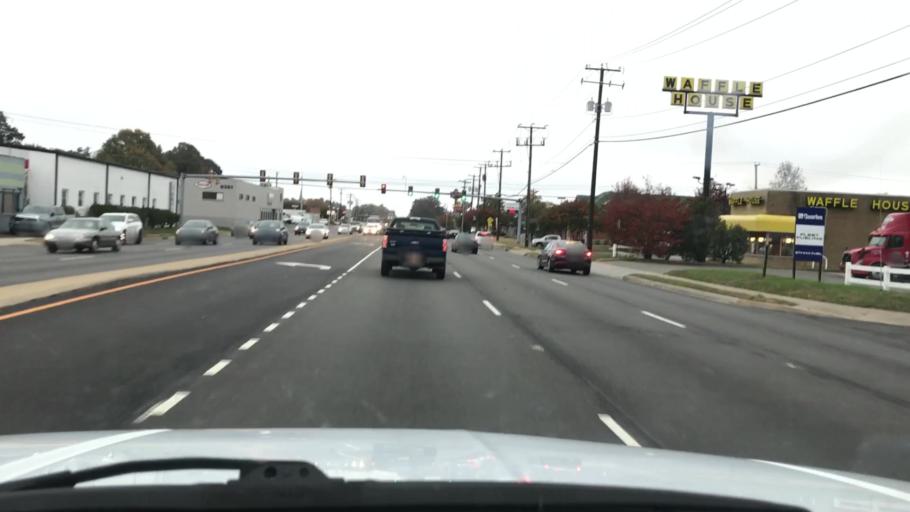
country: US
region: Virginia
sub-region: Henrico County
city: Chamberlayne
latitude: 37.6389
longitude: -77.4597
